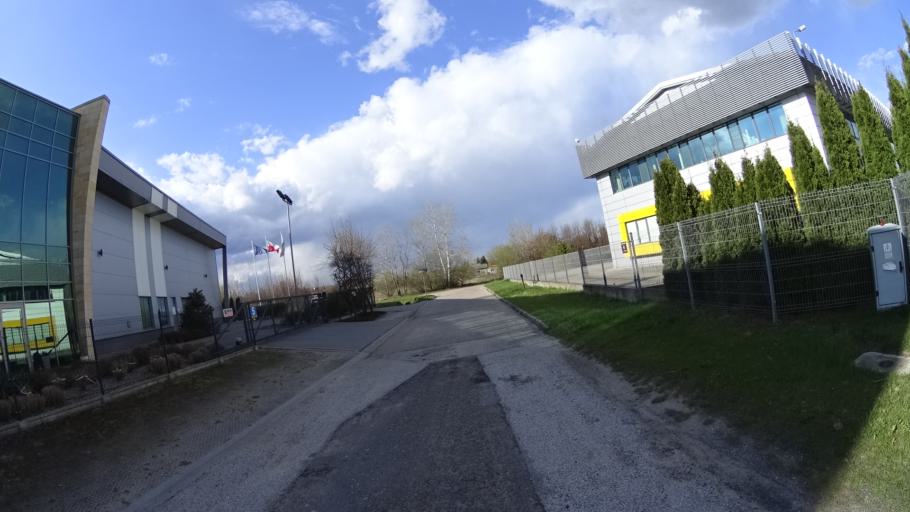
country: PL
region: Masovian Voivodeship
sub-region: Powiat warszawski zachodni
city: Babice
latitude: 52.2851
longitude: 20.8707
